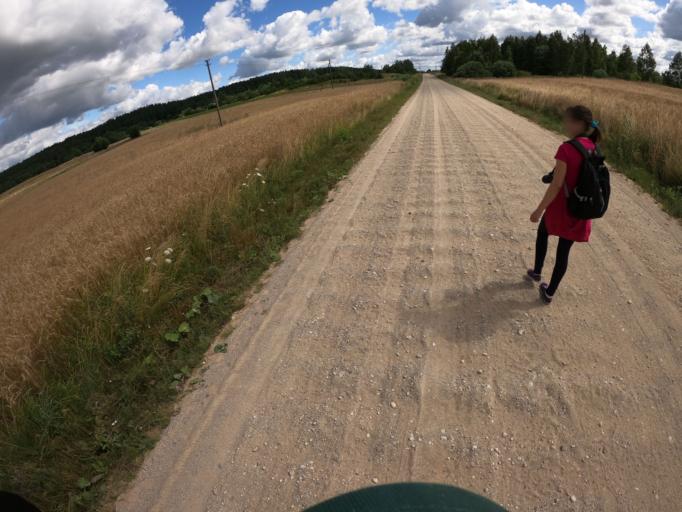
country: LT
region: Alytaus apskritis
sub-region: Alytus
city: Alytus
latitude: 54.3306
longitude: 24.0738
